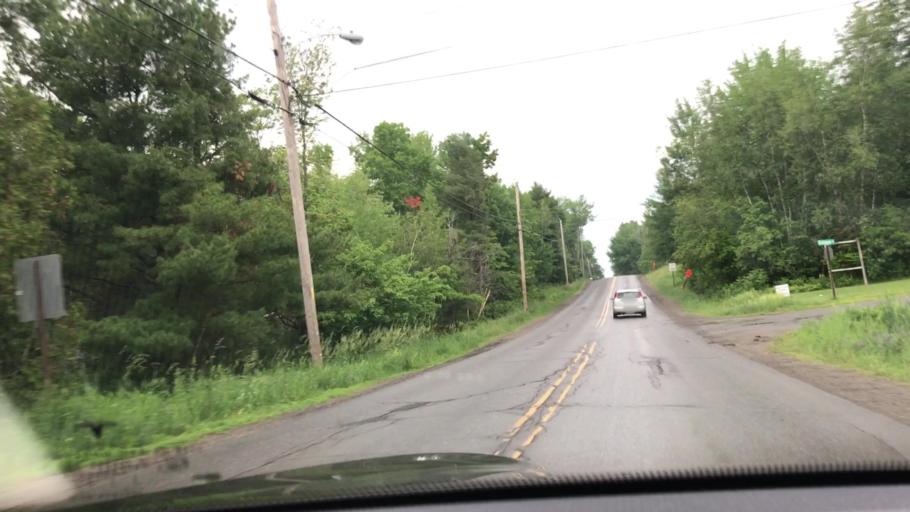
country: US
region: Maine
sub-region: Penobscot County
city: Orono
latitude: 44.8952
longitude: -68.6993
